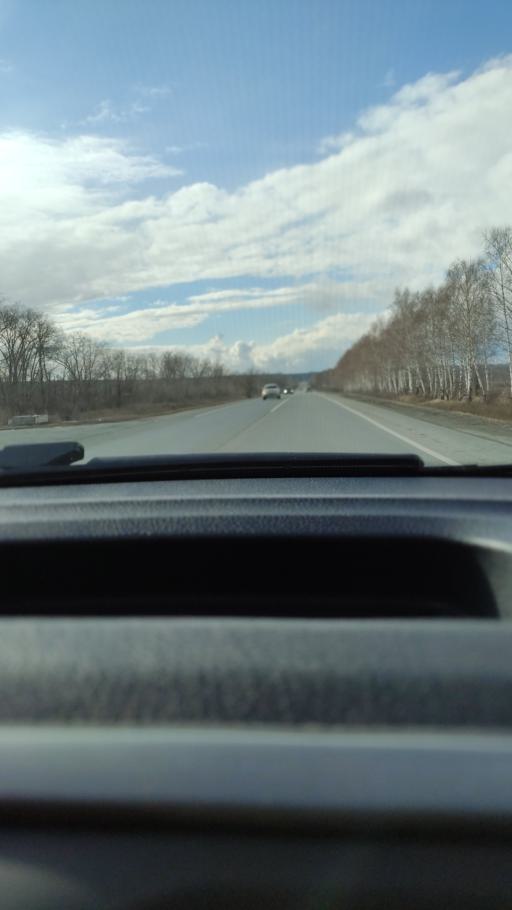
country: RU
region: Samara
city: Kurumoch
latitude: 53.4865
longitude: 50.0116
